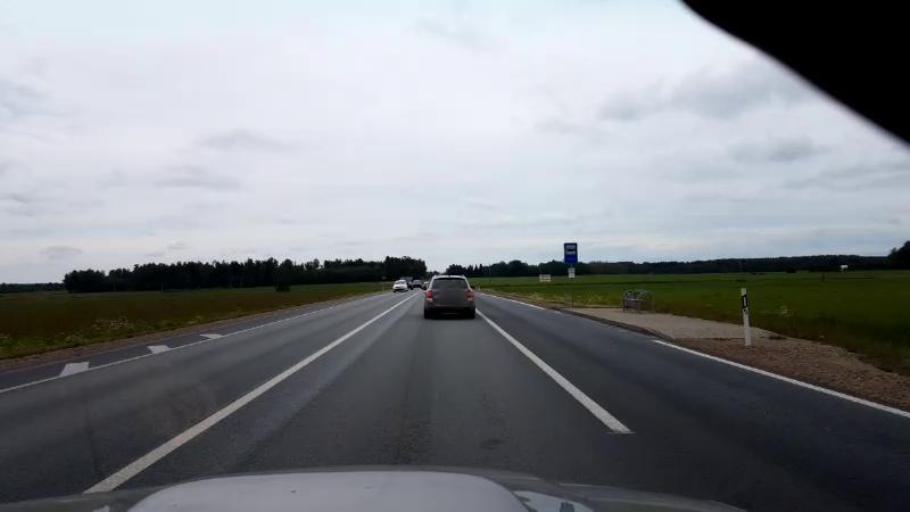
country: LV
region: Lecava
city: Iecava
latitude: 56.6498
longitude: 24.2290
